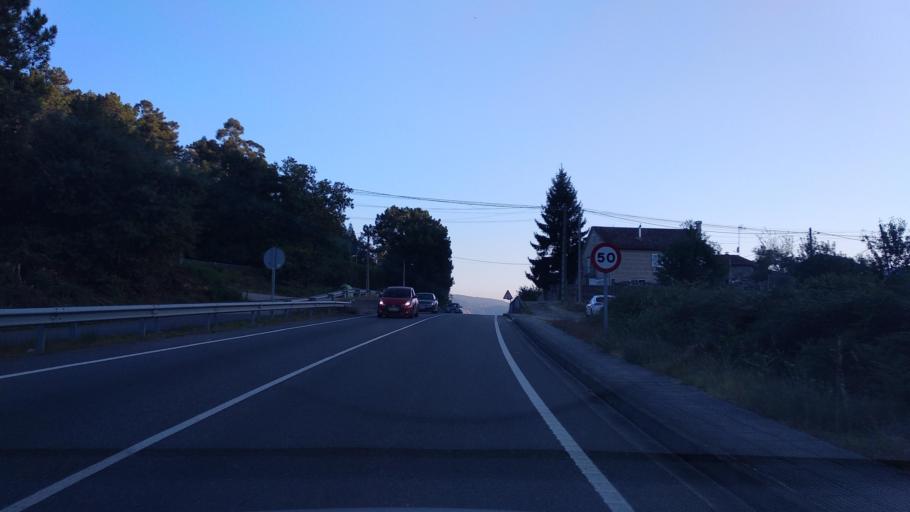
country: ES
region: Galicia
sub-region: Provincia de Pontevedra
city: Redondela
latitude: 42.3327
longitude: -8.6463
